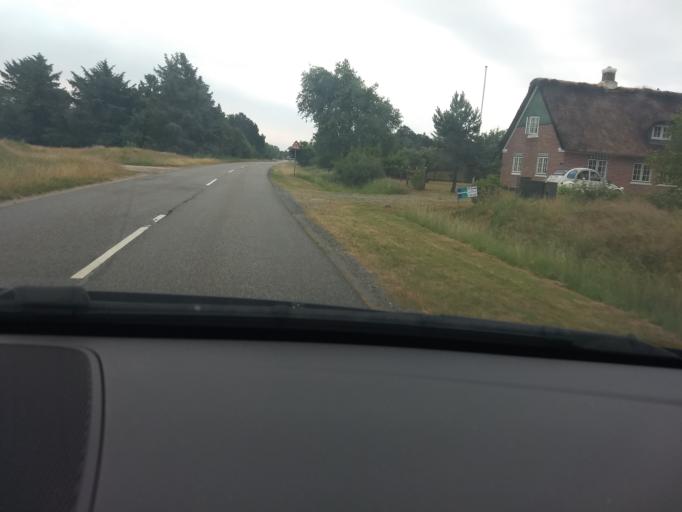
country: DK
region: South Denmark
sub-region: Fano Kommune
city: Nordby
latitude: 55.3563
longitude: 8.4643
